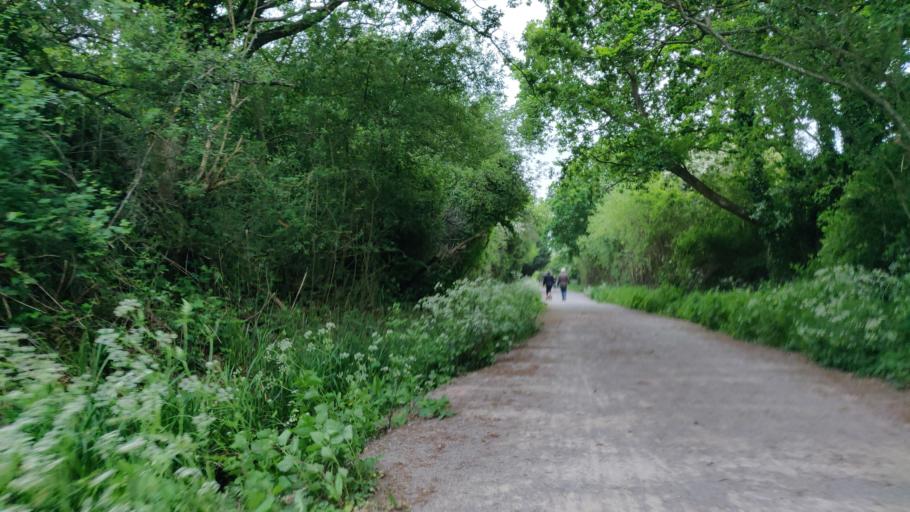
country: GB
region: England
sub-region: West Sussex
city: Partridge Green
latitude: 50.9602
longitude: -0.3107
